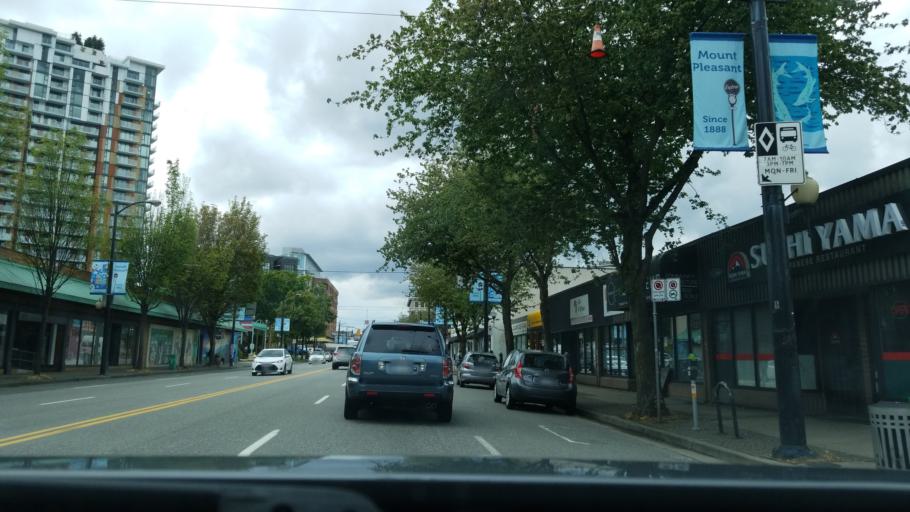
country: CA
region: British Columbia
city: Vancouver
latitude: 49.2628
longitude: -123.0970
